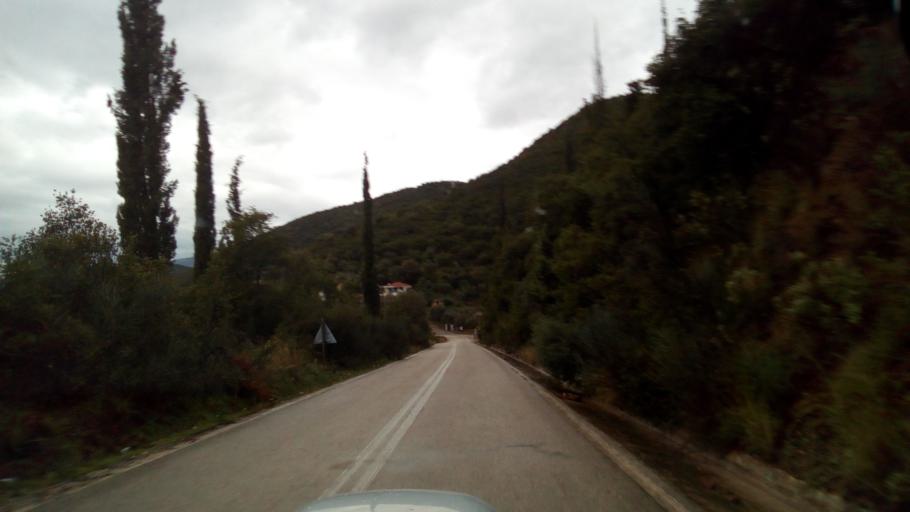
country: GR
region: West Greece
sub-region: Nomos Aitolias kai Akarnanias
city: Nafpaktos
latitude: 38.4262
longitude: 21.9327
